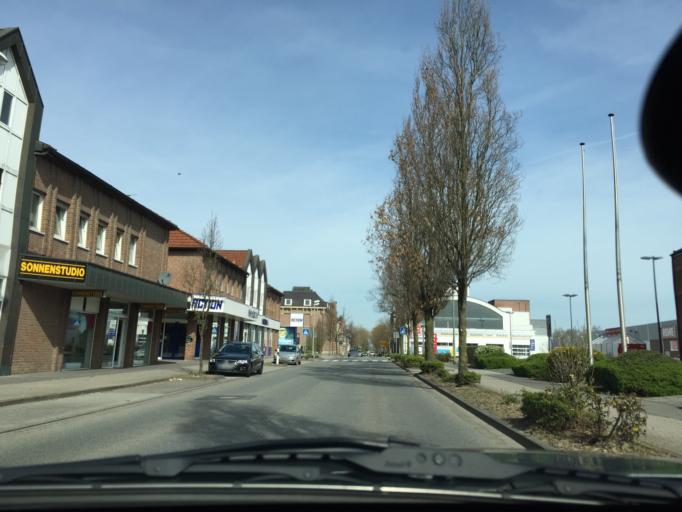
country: DE
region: North Rhine-Westphalia
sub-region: Regierungsbezirk Dusseldorf
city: Goch
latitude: 51.6832
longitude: 6.1598
